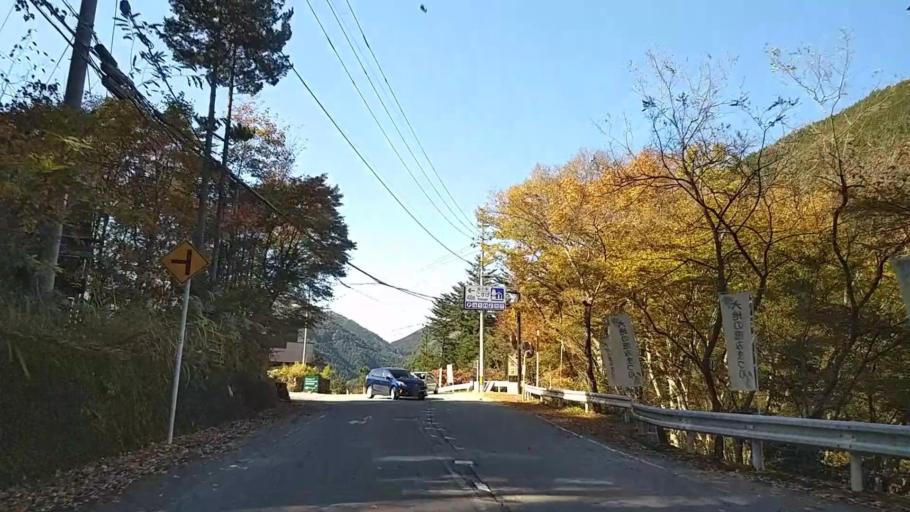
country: JP
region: Yamanashi
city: Otsuki
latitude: 35.7559
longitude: 138.9520
